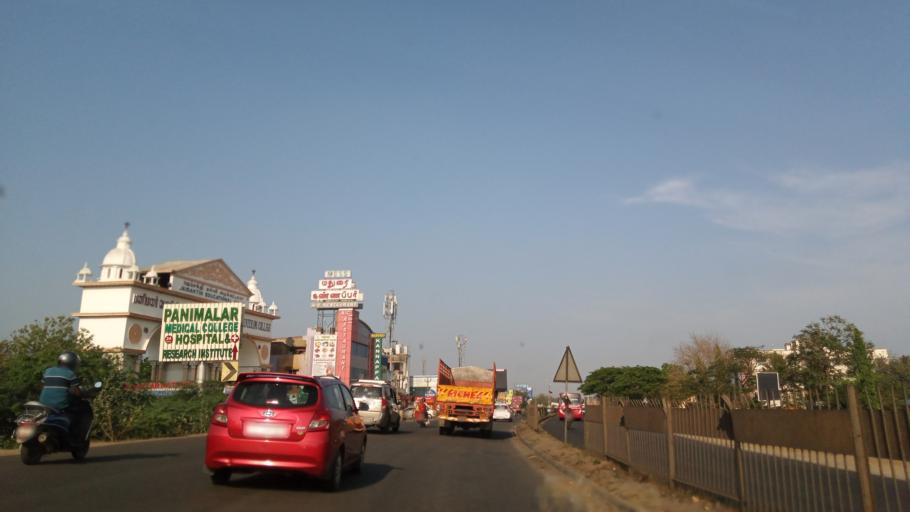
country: IN
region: Tamil Nadu
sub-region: Kancheepuram
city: Poonamalle
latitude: 13.0469
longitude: 80.0749
